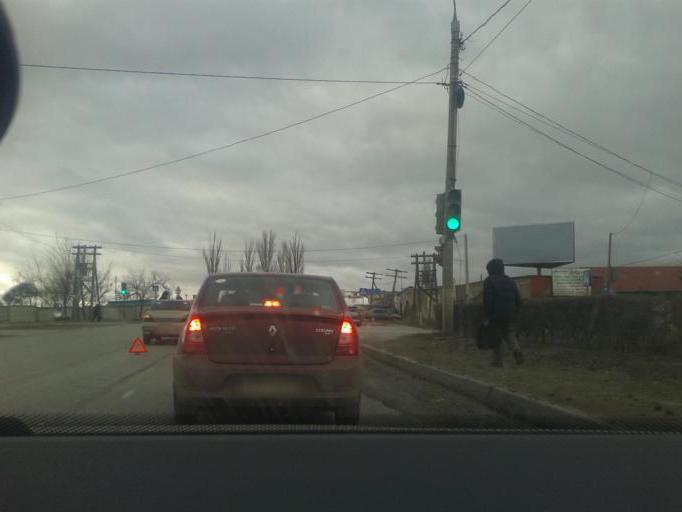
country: RU
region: Volgograd
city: Volgograd
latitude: 48.7027
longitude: 44.4558
